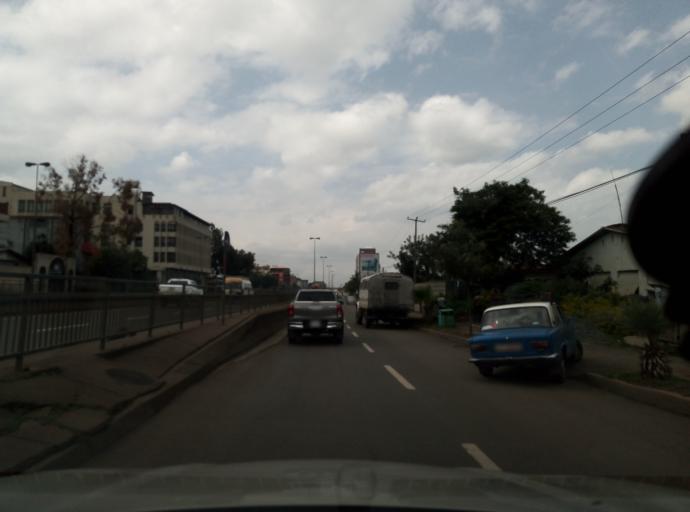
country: ET
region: Adis Abeba
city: Addis Ababa
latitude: 9.0041
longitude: 38.7187
